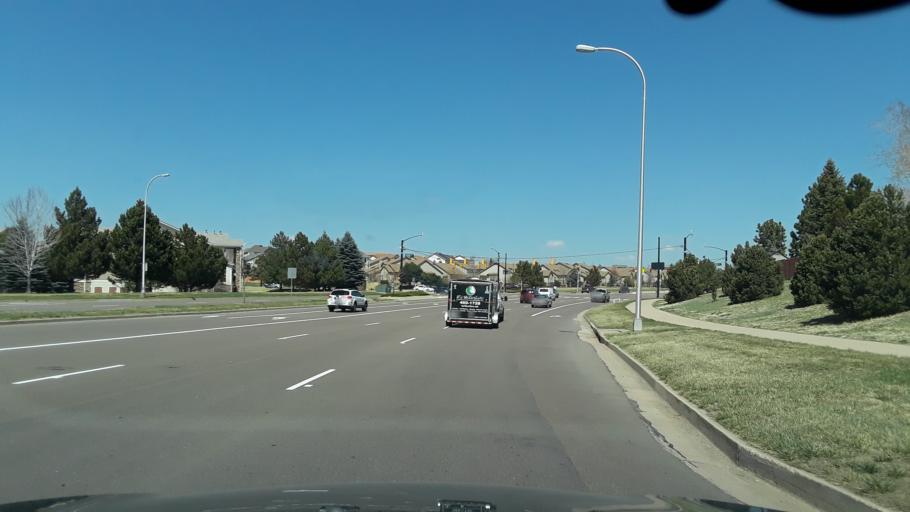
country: US
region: Colorado
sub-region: El Paso County
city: Cimarron Hills
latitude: 38.9304
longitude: -104.7416
